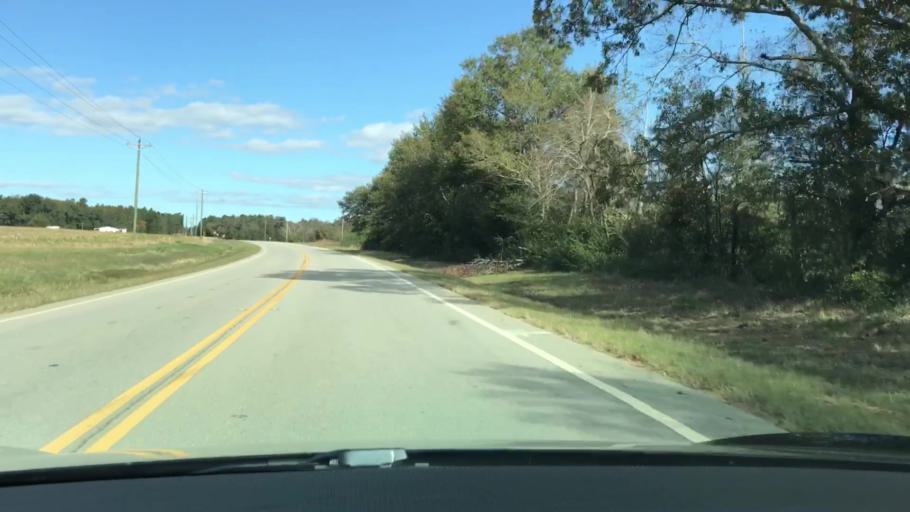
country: US
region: Georgia
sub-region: Jefferson County
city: Wrens
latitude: 33.1795
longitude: -82.4533
